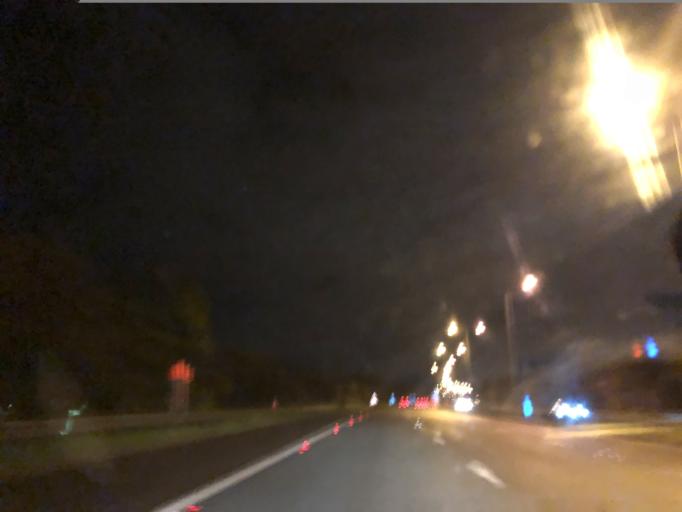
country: GB
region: England
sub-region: Kirklees
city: Cleckheaton
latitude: 53.7485
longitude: -1.7378
